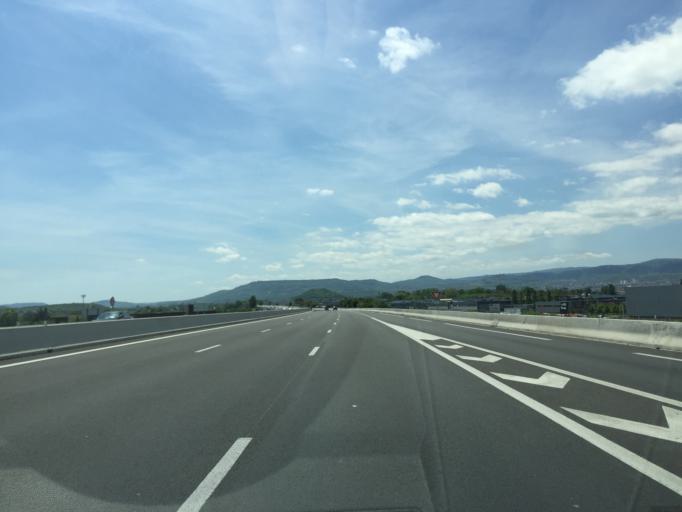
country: FR
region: Auvergne
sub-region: Departement du Puy-de-Dome
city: Aulnat
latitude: 45.8036
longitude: 3.1499
